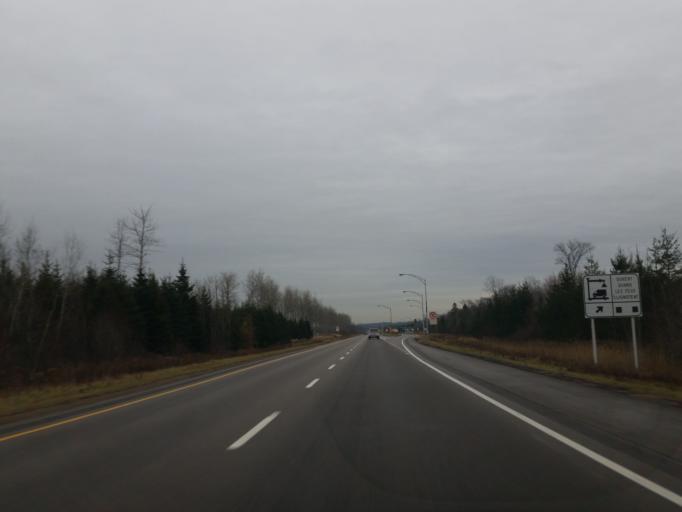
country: CA
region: Quebec
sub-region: Capitale-Nationale
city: Neuville
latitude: 46.7457
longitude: -71.5274
